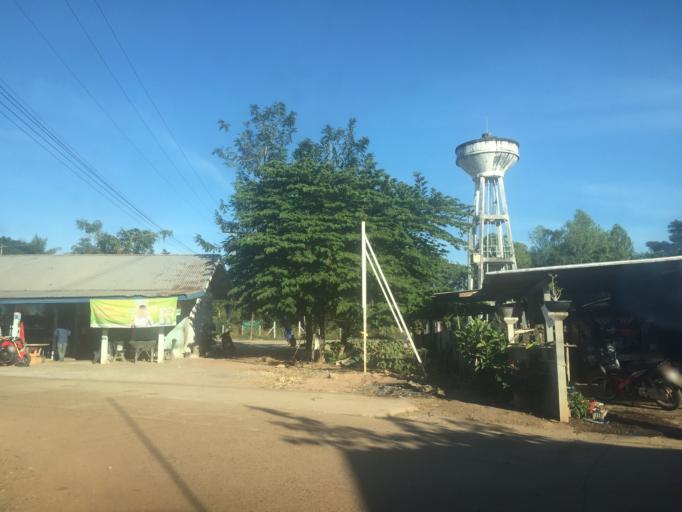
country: TH
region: Changwat Udon Thani
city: Si That
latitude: 16.9684
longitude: 103.2314
